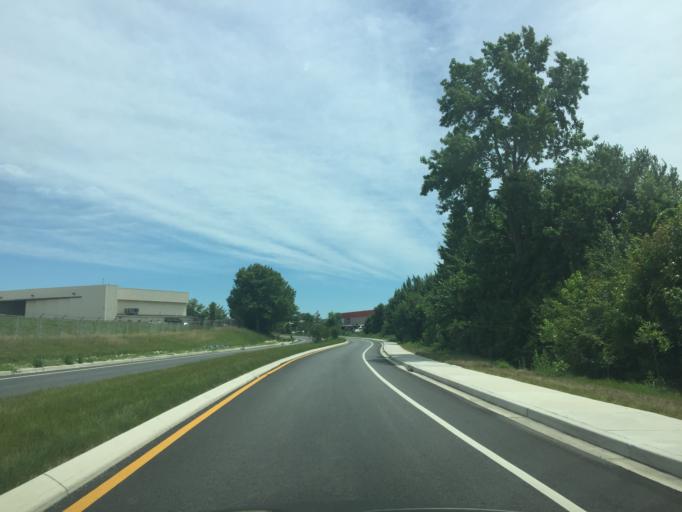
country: US
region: Maryland
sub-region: Baltimore County
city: Middle River
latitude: 39.3331
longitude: -76.4277
